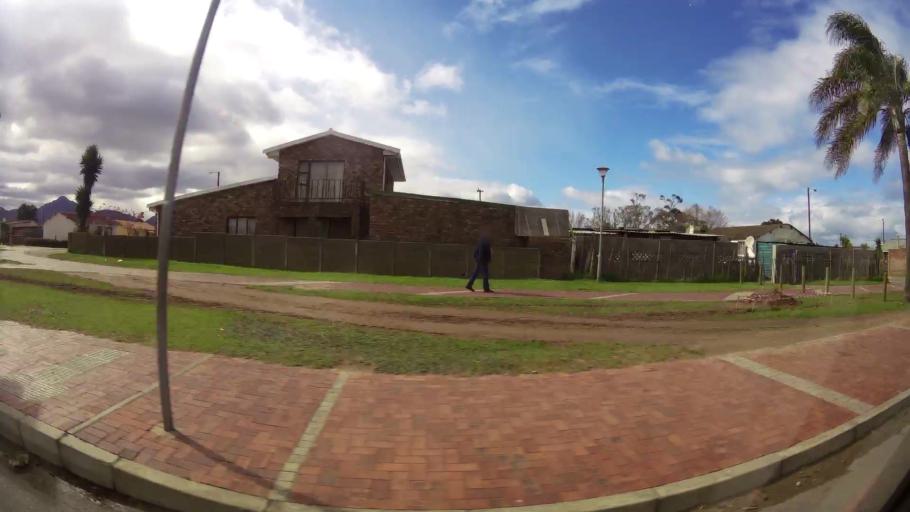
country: ZA
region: Western Cape
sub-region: Eden District Municipality
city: George
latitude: -33.9880
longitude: 22.4736
